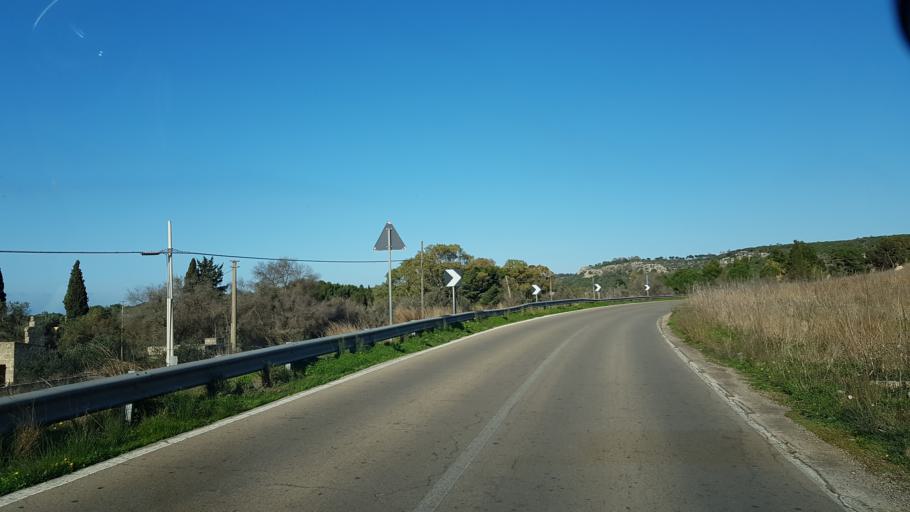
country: IT
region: Apulia
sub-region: Provincia di Lecce
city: Sannicola
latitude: 40.0985
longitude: 18.0203
